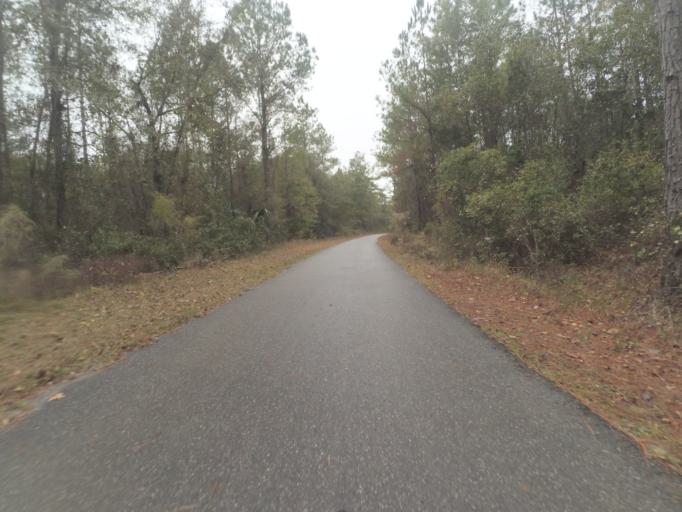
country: US
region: Florida
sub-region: Alachua County
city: Hawthorne
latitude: 29.5883
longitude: -82.1256
